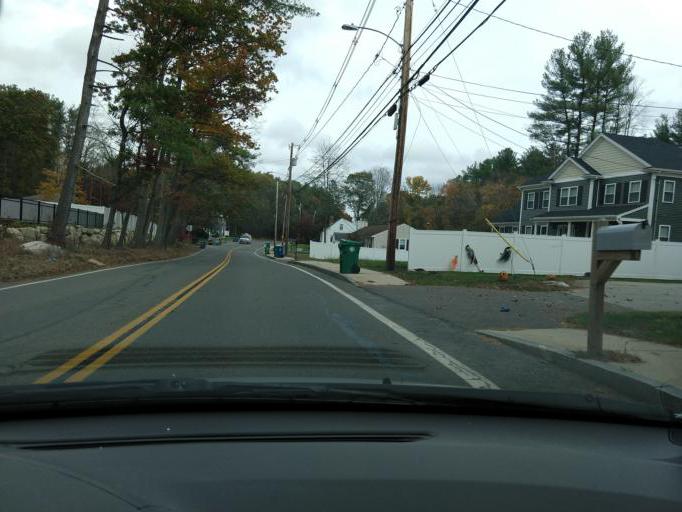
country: US
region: Massachusetts
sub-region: Middlesex County
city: Pinehurst
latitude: 42.5029
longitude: -71.2245
